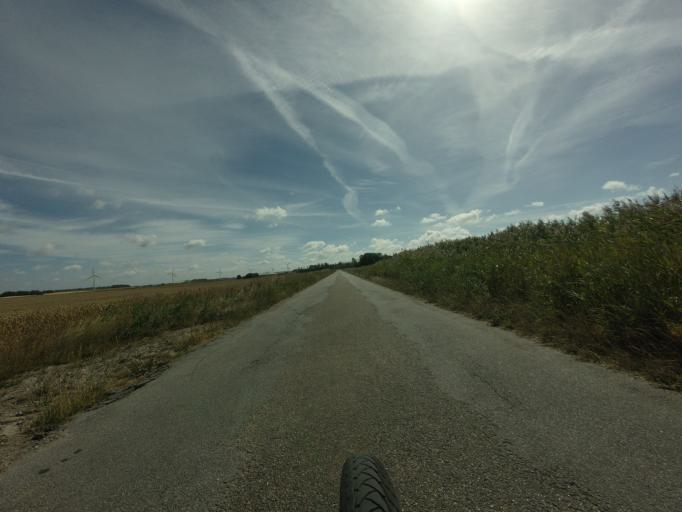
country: DK
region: North Denmark
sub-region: Hjorring Kommune
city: Vra
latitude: 57.3409
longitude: 9.8034
